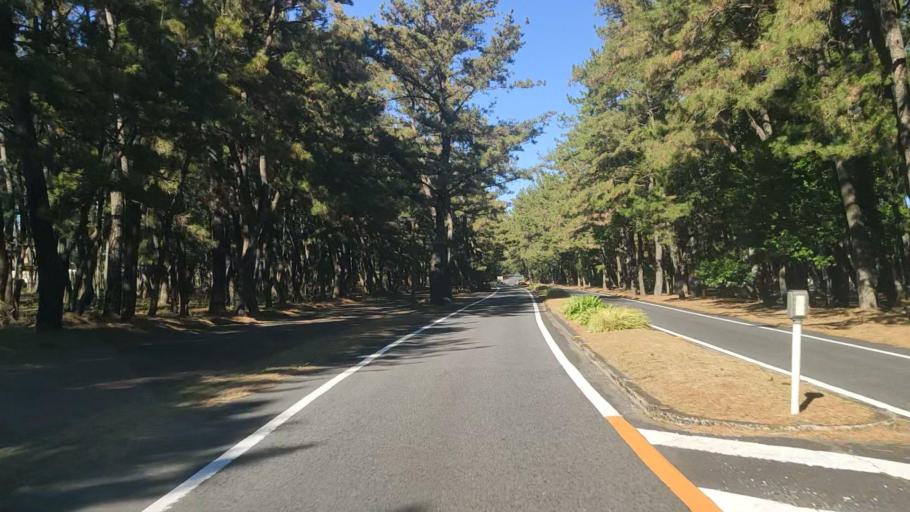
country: JP
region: Miyazaki
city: Miyazaki-shi
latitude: 31.9410
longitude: 131.4648
